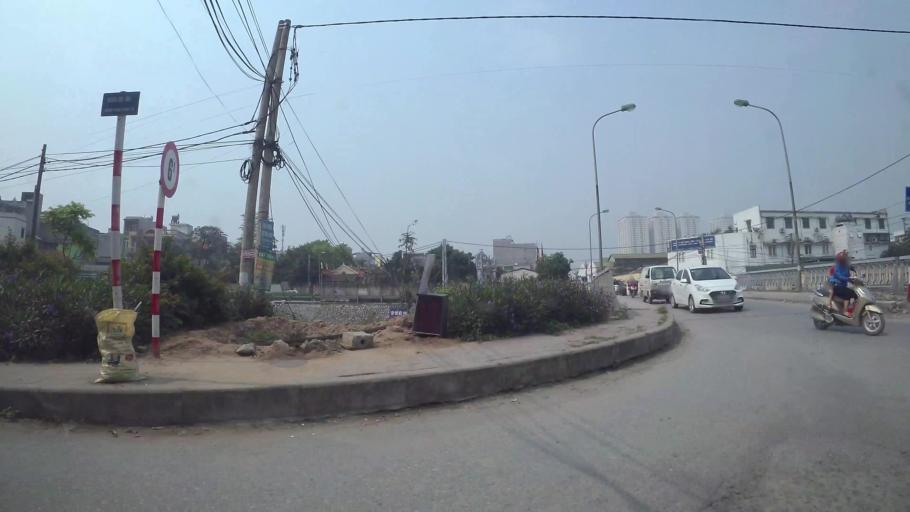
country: VN
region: Ha Noi
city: Van Dien
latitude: 20.9600
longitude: 105.8136
